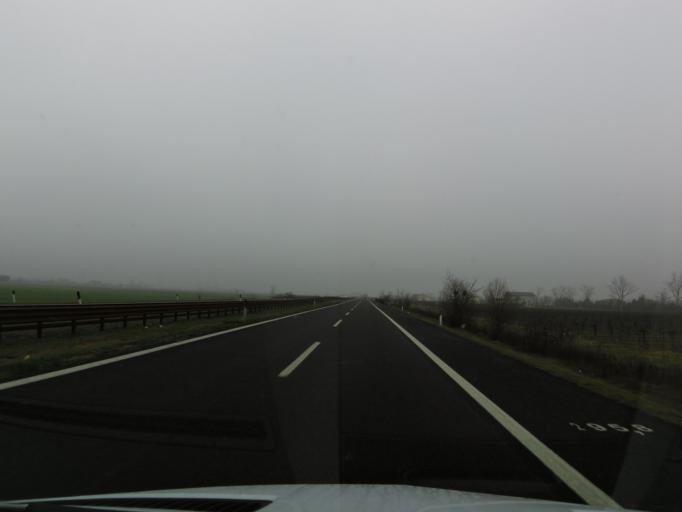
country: IT
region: Emilia-Romagna
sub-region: Provincia di Modena
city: Migliarina
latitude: 44.8217
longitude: 10.8518
